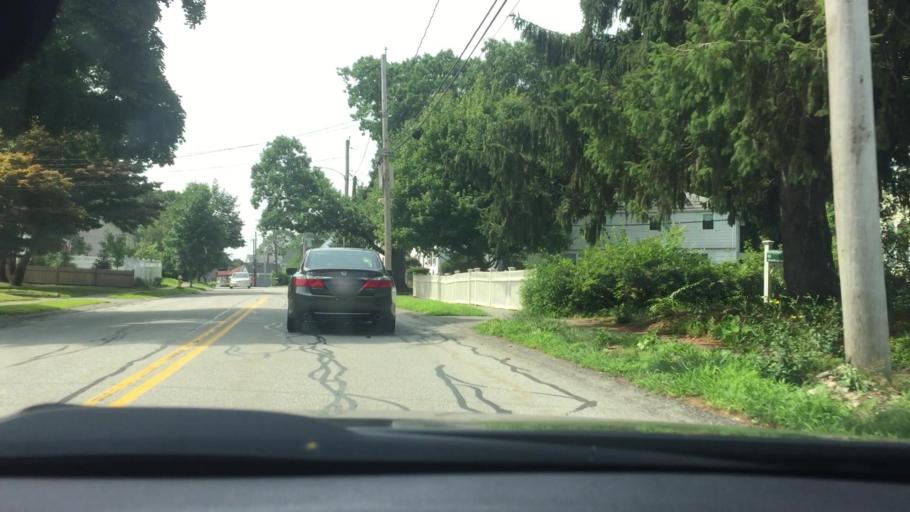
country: US
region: Massachusetts
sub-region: Norfolk County
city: Needham
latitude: 42.2981
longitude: -71.2362
